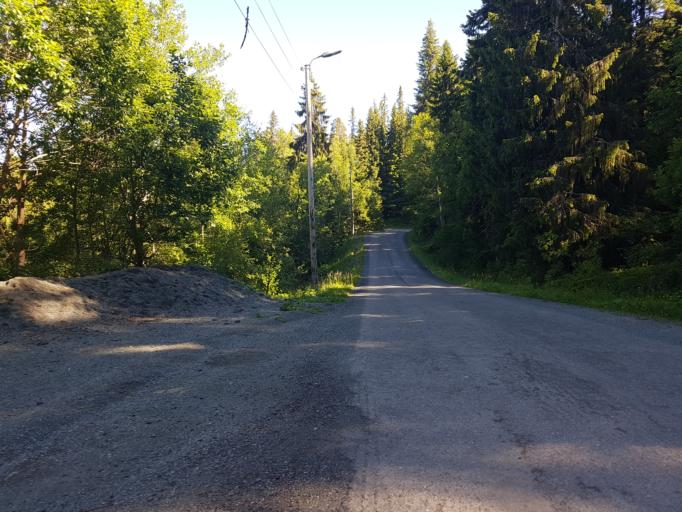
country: NO
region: Sor-Trondelag
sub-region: Trondheim
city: Trondheim
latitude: 63.4301
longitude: 10.2770
